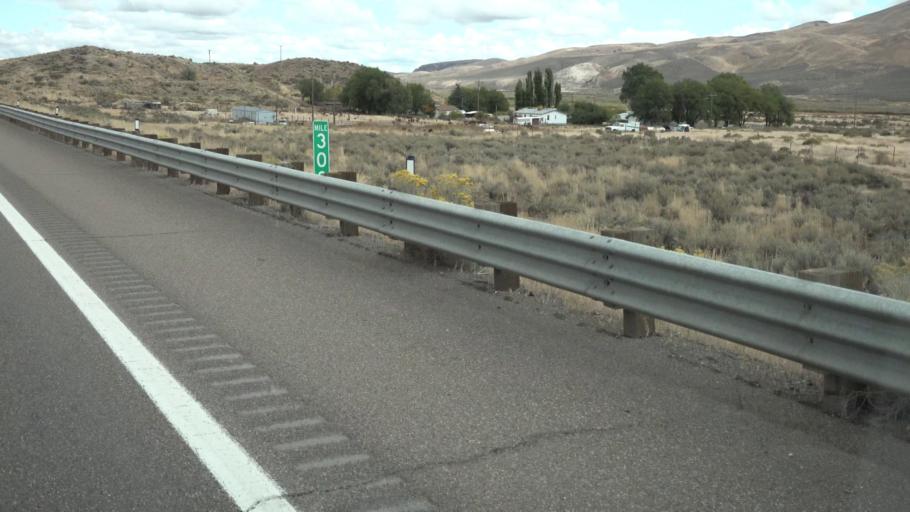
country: US
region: Nevada
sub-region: Elko County
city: Elko
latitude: 40.9049
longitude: -115.7008
